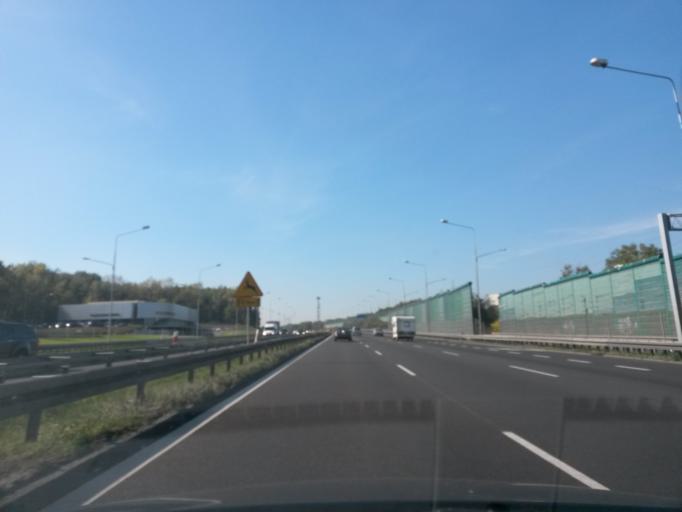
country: PL
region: Silesian Voivodeship
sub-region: Chorzow
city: Chorzow
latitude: 50.2550
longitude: 18.9728
